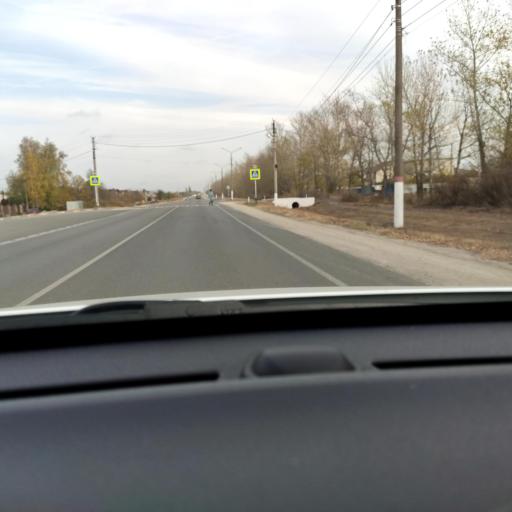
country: RU
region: Voronezj
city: Novaya Usman'
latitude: 51.6517
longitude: 39.4256
